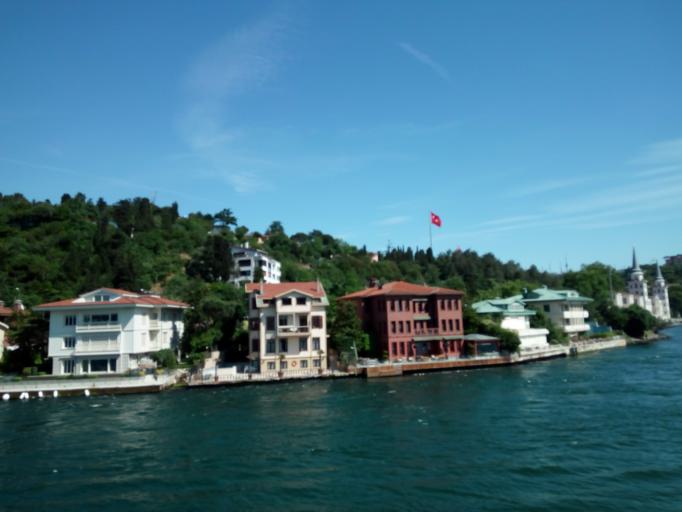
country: TR
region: Istanbul
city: UEskuedar
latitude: 41.0623
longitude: 29.0518
